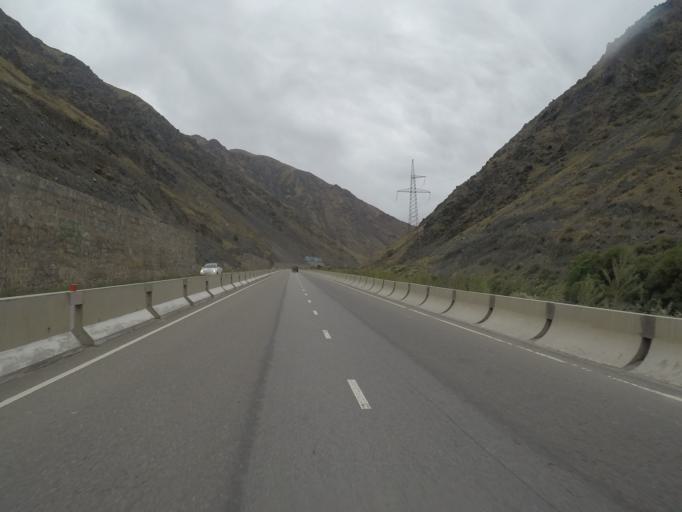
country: KG
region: Chuy
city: Bystrovka
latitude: 42.5699
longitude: 75.8107
